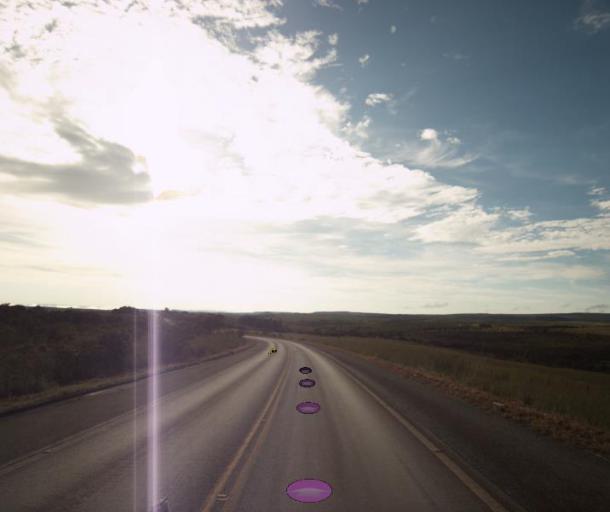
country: BR
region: Goias
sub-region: Pirenopolis
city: Pirenopolis
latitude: -15.7680
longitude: -48.7182
